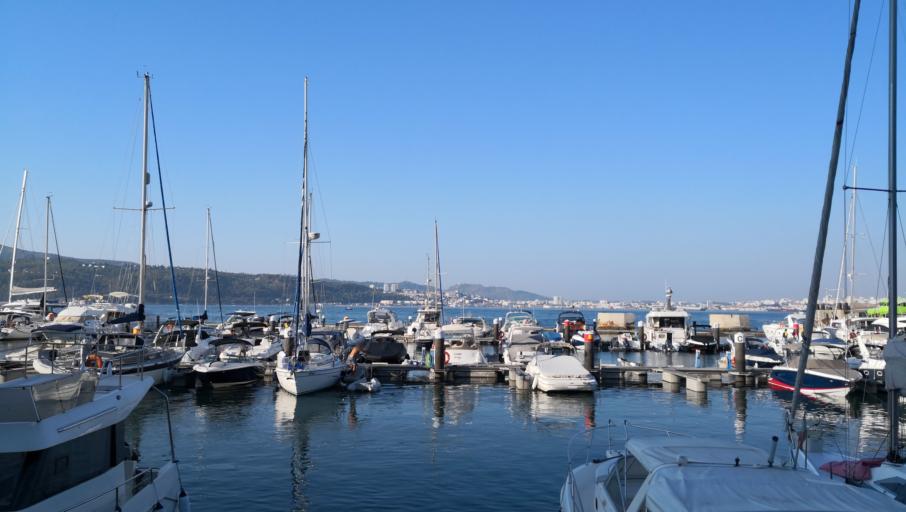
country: PT
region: Setubal
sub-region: Setubal
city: Setubal
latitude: 38.4933
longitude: -8.9023
